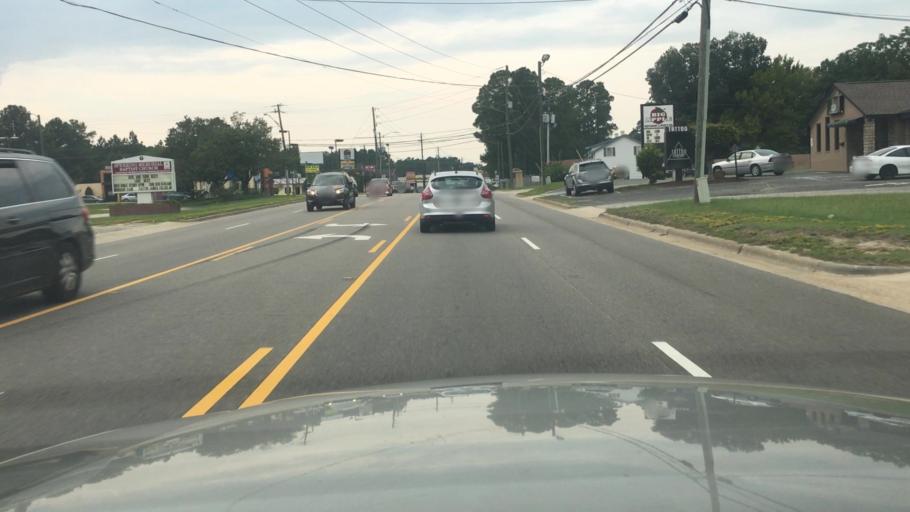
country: US
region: North Carolina
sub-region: Cumberland County
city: Fort Bragg
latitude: 35.0935
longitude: -78.9857
